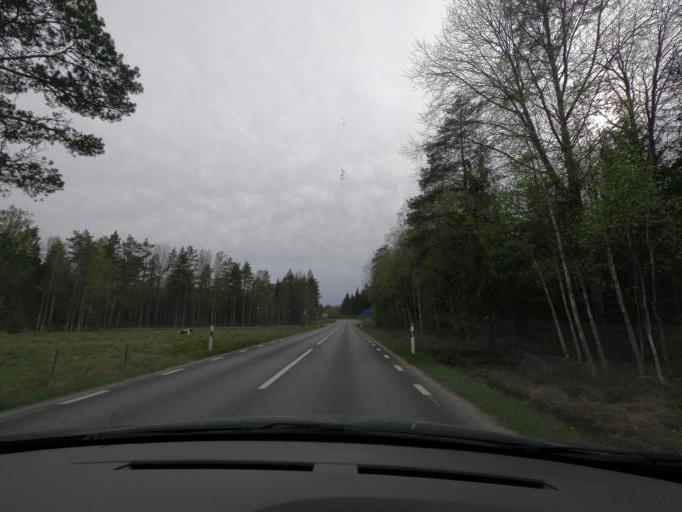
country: SE
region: Joenkoeping
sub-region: Varnamo Kommun
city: Bredaryd
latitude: 57.1850
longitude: 13.7531
